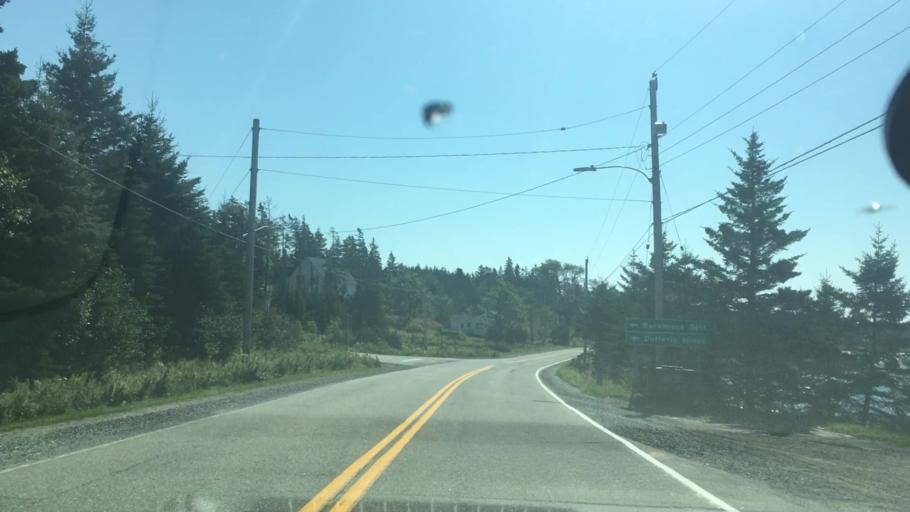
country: CA
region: Nova Scotia
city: New Glasgow
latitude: 44.9161
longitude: -62.3821
